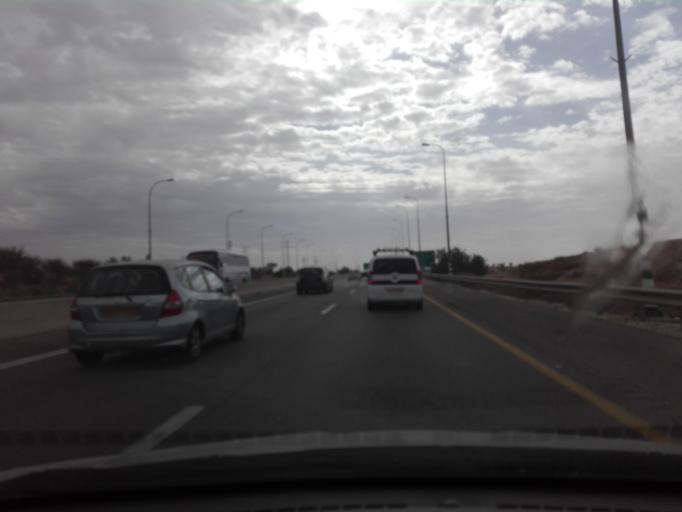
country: IL
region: Southern District
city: Lehavim
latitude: 31.3172
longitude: 34.7874
